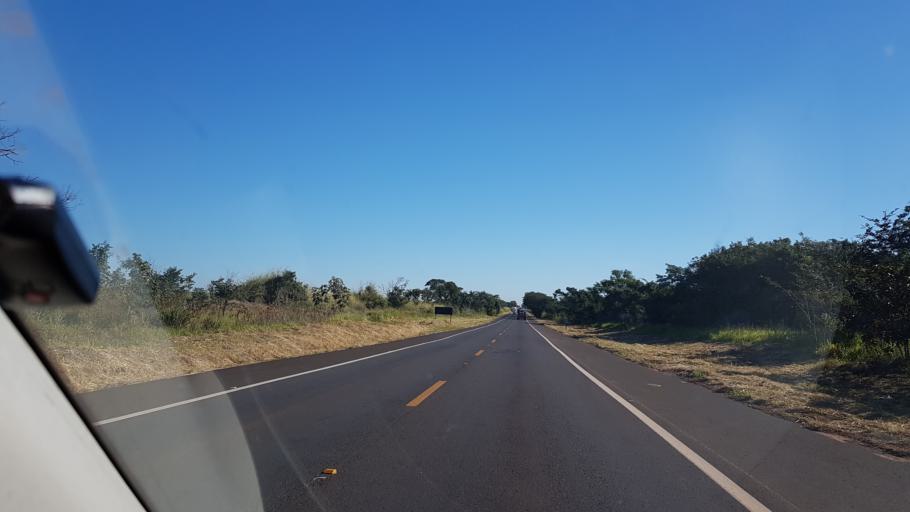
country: BR
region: Sao Paulo
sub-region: Maracai
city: Maracai
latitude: -22.5592
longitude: -50.5268
